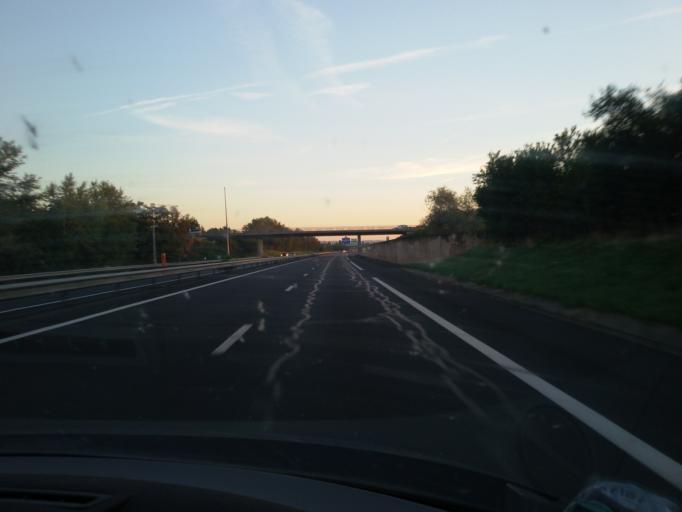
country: FR
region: Auvergne
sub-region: Departement du Puy-de-Dome
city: Menetrol
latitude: 45.8870
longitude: 3.1538
